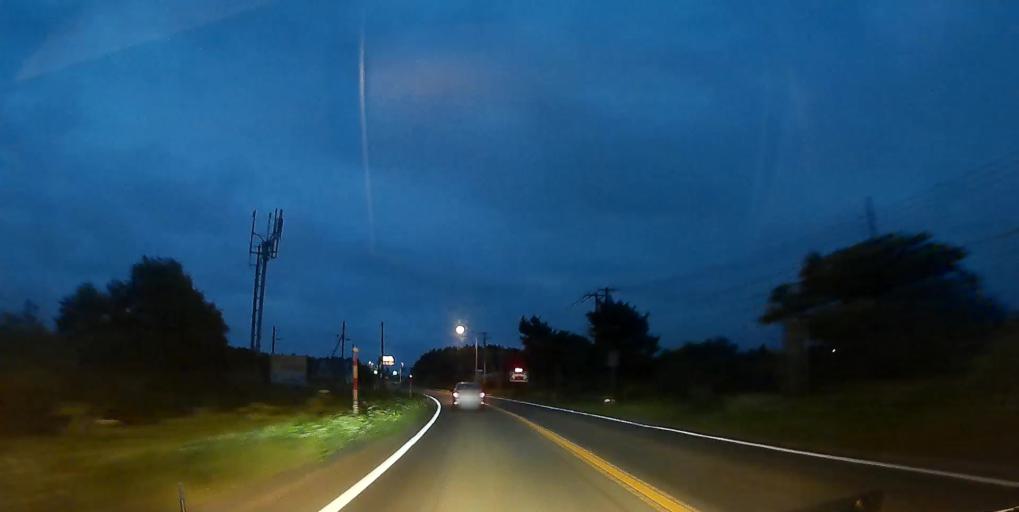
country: JP
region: Hokkaido
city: Nanae
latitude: 42.2091
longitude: 140.3968
